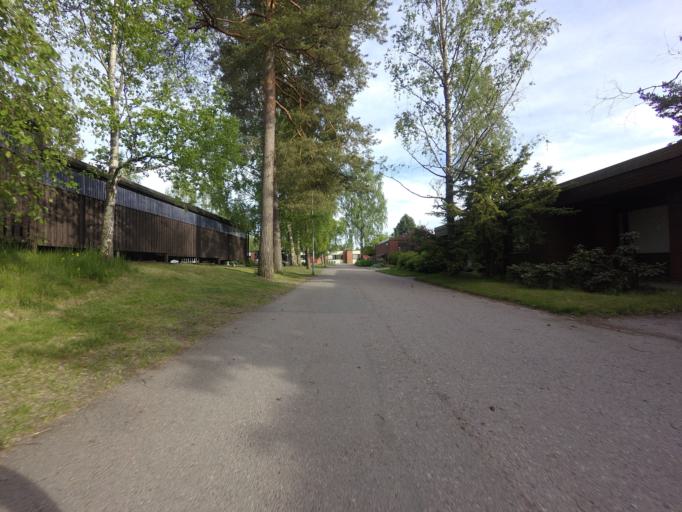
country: FI
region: Uusimaa
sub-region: Helsinki
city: Koukkuniemi
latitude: 60.1529
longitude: 24.7508
